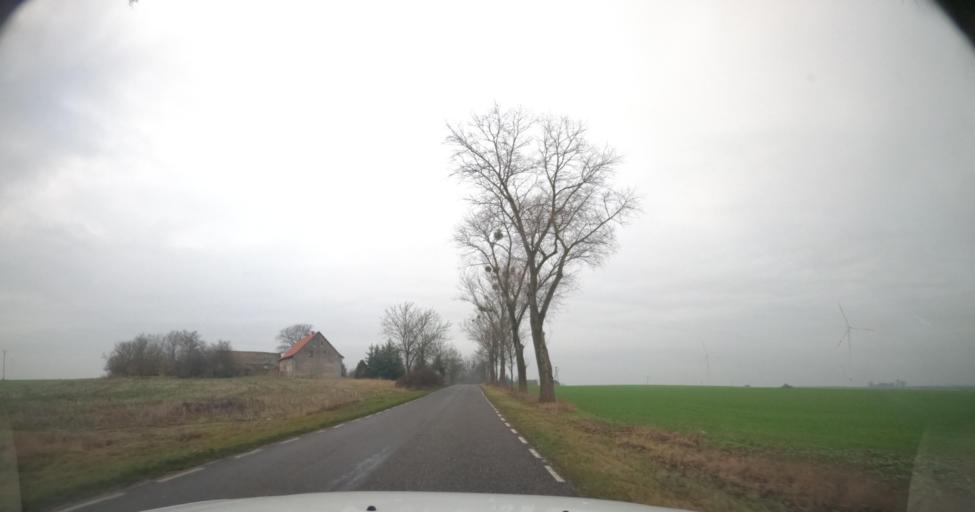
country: PL
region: West Pomeranian Voivodeship
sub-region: Powiat mysliborski
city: Boleszkowice
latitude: 52.7385
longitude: 14.6013
